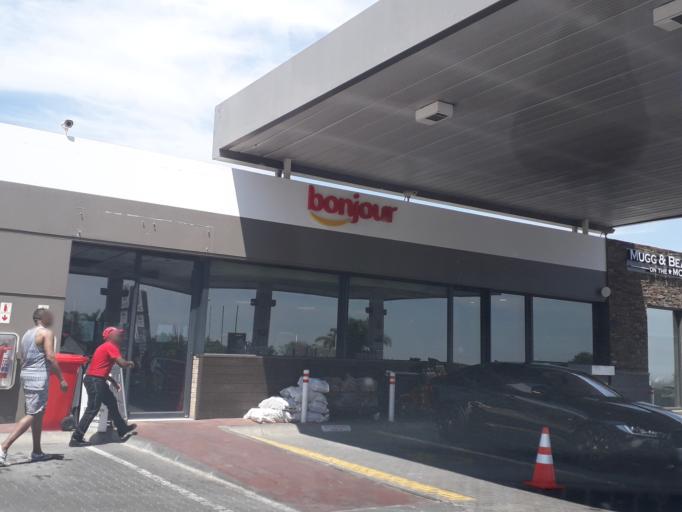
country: ZA
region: Gauteng
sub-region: City of Johannesburg Metropolitan Municipality
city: Diepsloot
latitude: -26.0407
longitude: 27.9909
